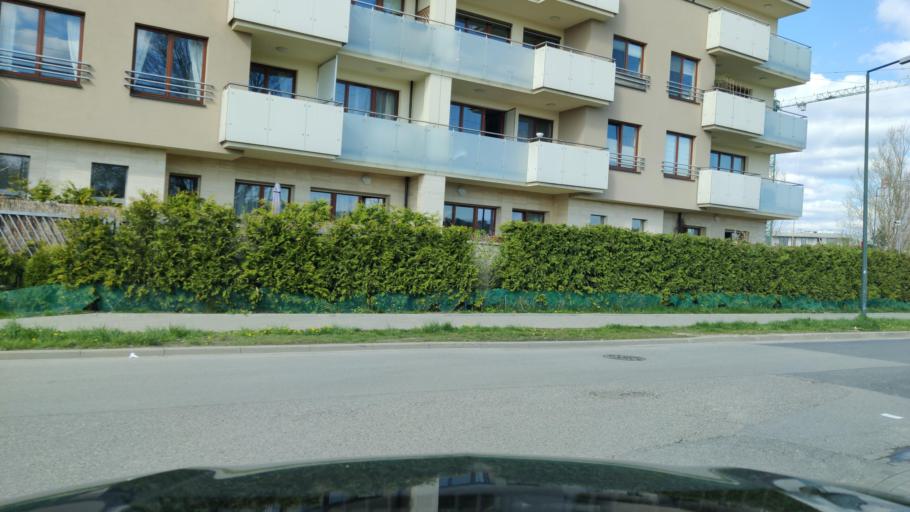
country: PL
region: Masovian Voivodeship
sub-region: Warszawa
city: Kabaty
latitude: 52.1270
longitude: 21.0683
